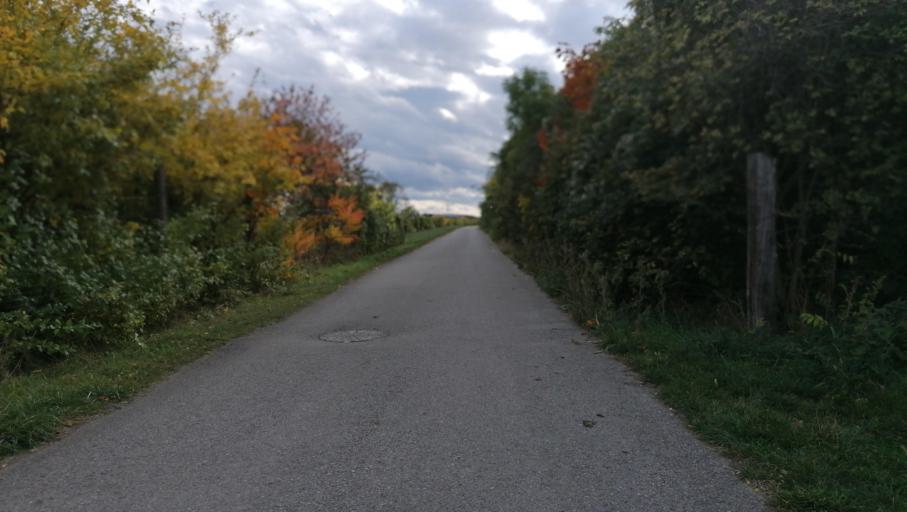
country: AT
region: Lower Austria
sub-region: Politischer Bezirk Baden
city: Tattendorf
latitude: 47.9572
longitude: 16.3091
